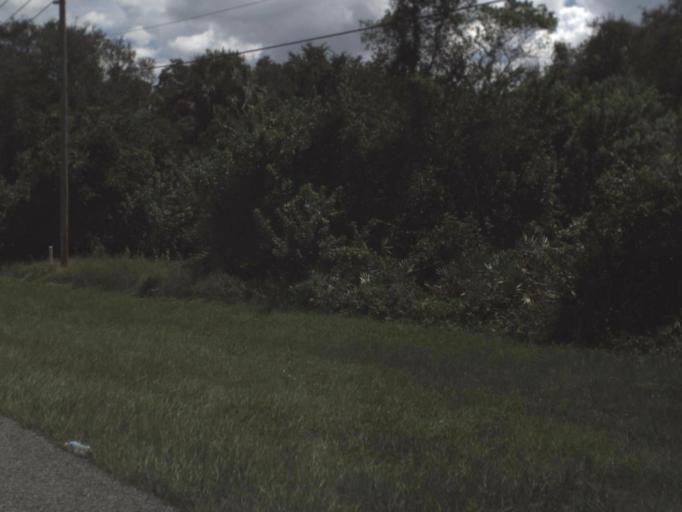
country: US
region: Florida
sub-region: Polk County
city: Babson Park
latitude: 27.8850
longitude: -81.4579
